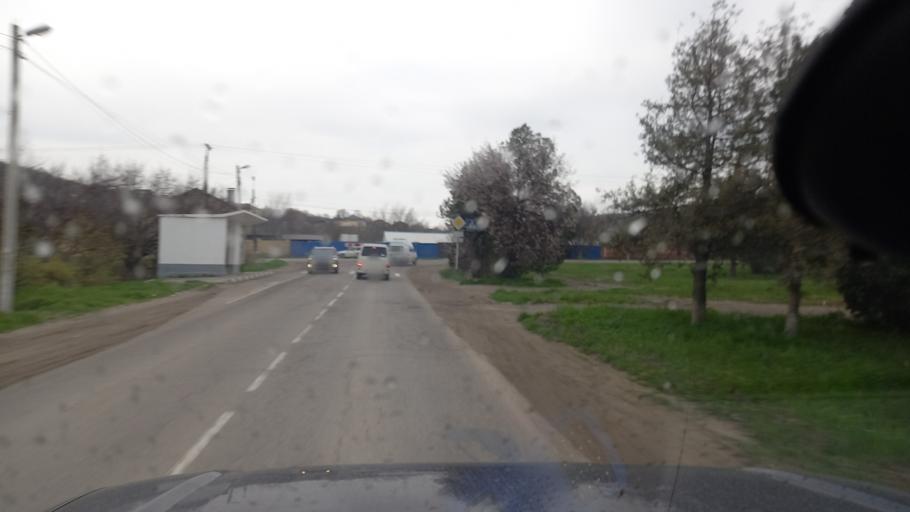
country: RU
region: Krasnodarskiy
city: Sukko
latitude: 44.8609
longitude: 37.4398
